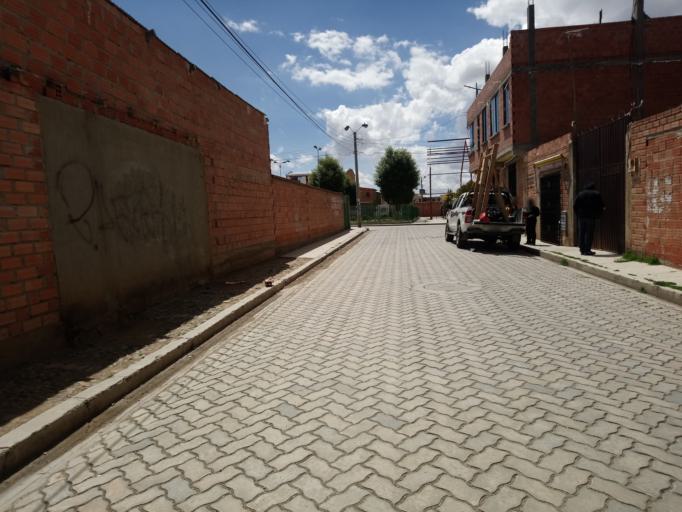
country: BO
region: La Paz
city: La Paz
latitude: -16.5563
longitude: -68.1928
